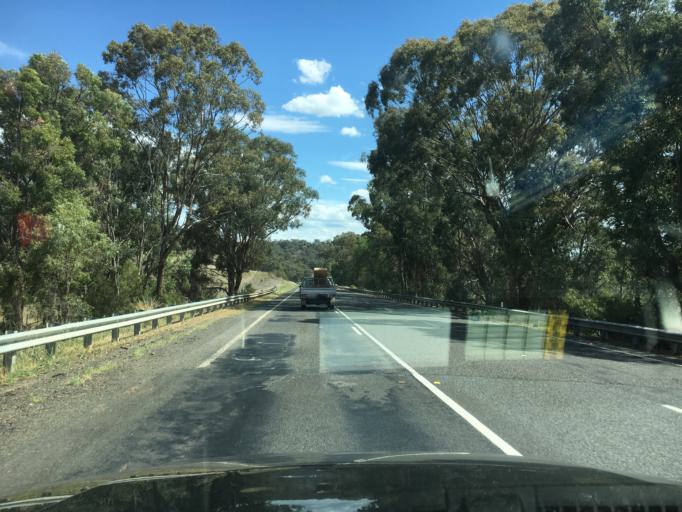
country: AU
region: New South Wales
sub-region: Liverpool Plains
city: Quirindi
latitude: -31.5167
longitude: 150.8526
